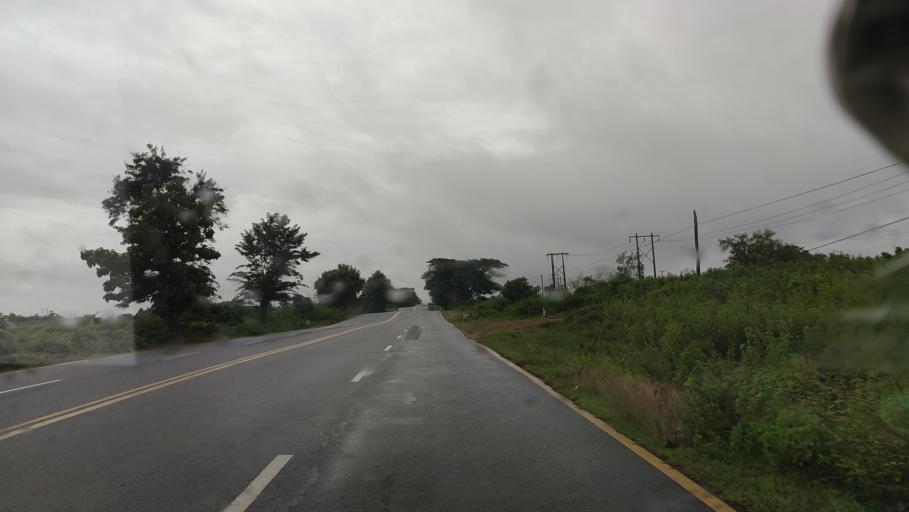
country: MM
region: Mandalay
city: Pyinmana
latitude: 19.9422
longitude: 96.2526
